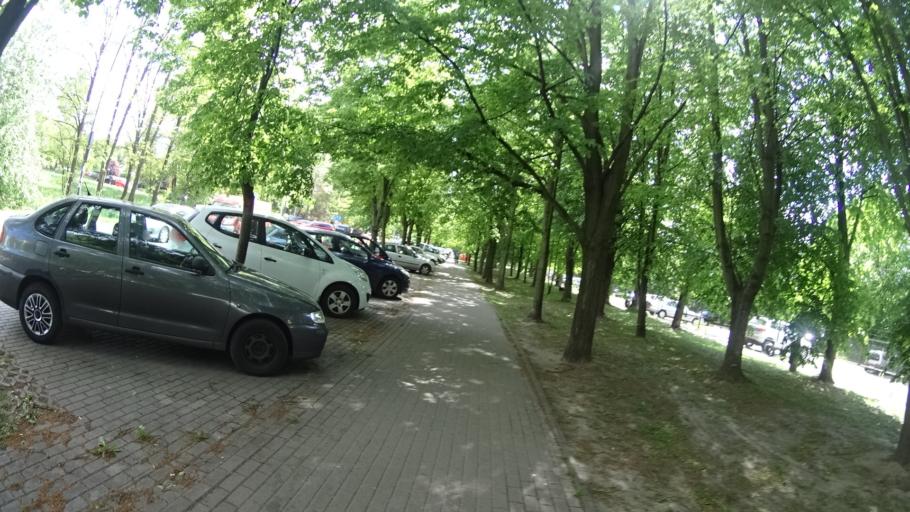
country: PL
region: Masovian Voivodeship
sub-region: Warszawa
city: Bielany
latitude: 52.2795
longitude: 20.9182
